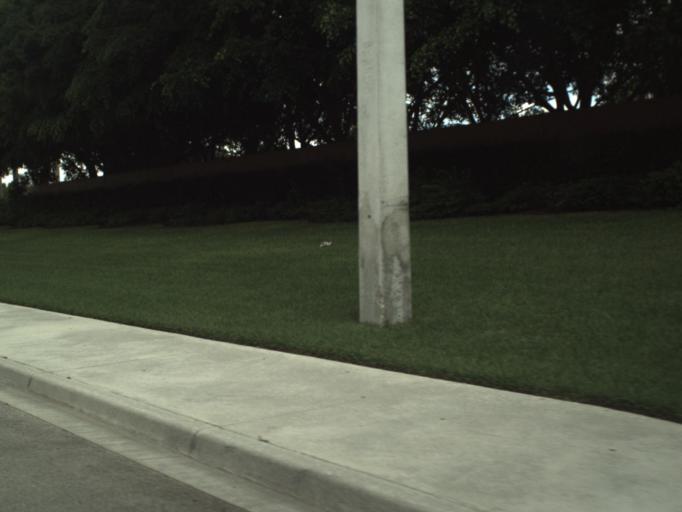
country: US
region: Florida
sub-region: Palm Beach County
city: Wellington
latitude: 26.6508
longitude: -80.1975
